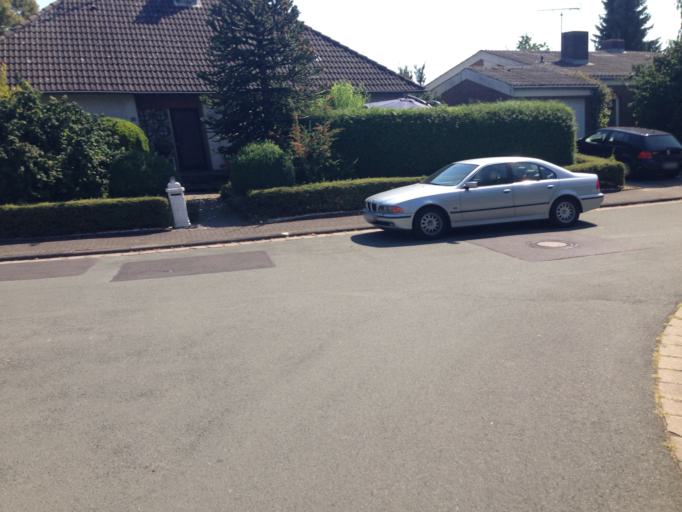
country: DE
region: Hesse
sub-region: Regierungsbezirk Giessen
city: Wetzlar
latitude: 50.5083
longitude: 8.5482
